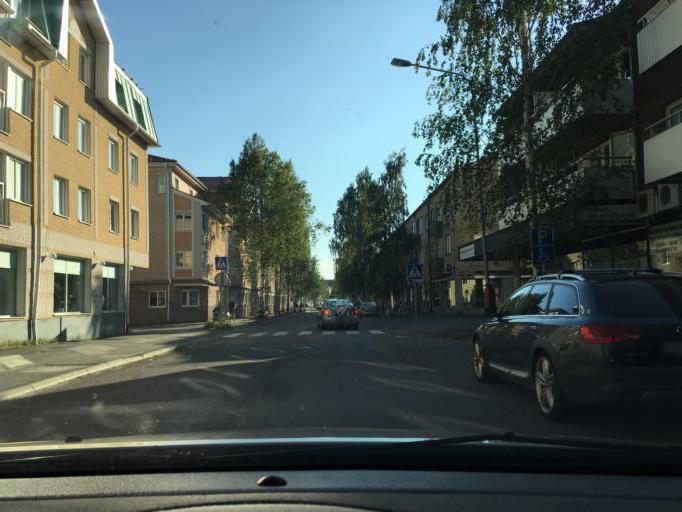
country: SE
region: Norrbotten
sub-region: Bodens Kommun
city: Boden
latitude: 65.8276
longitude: 21.7029
